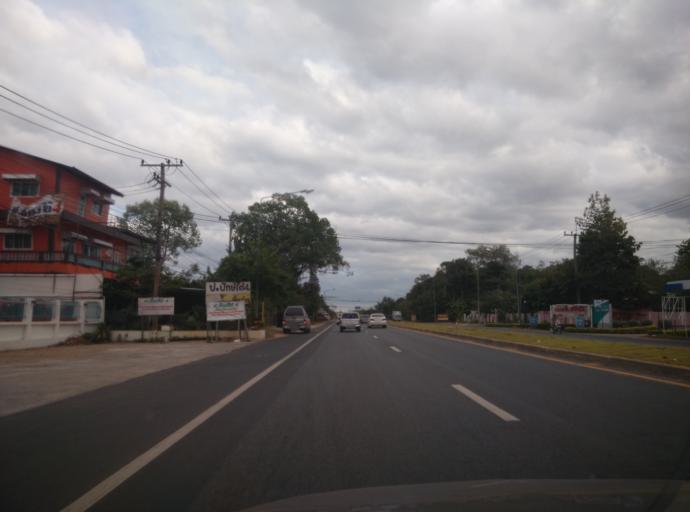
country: TH
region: Sisaket
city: Si Sa Ket
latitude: 15.1256
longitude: 104.2895
